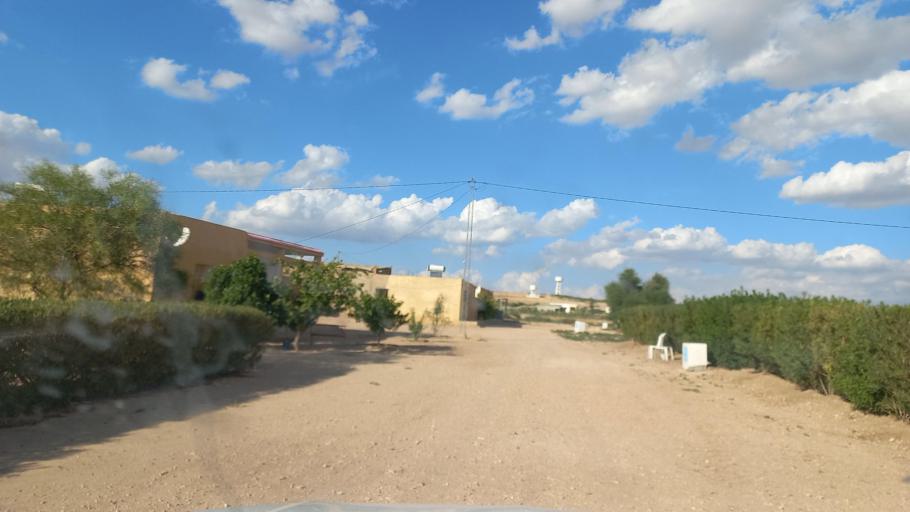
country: TN
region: Al Qasrayn
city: Sbiba
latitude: 35.3852
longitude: 9.0418
